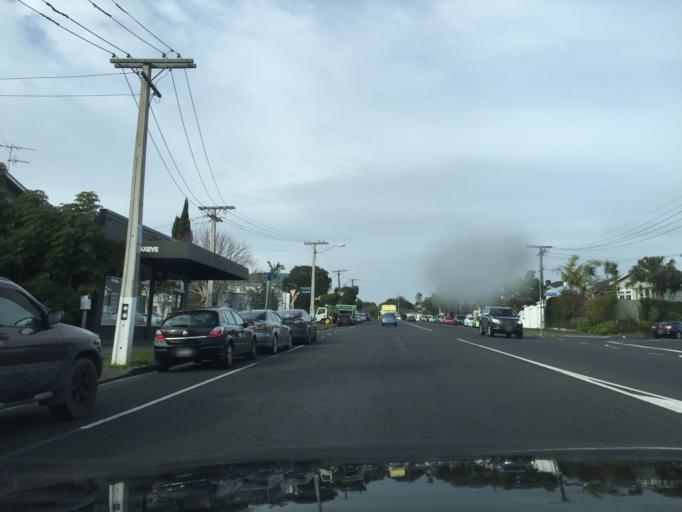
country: NZ
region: Auckland
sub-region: Auckland
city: Auckland
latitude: -36.8604
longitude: 174.7328
